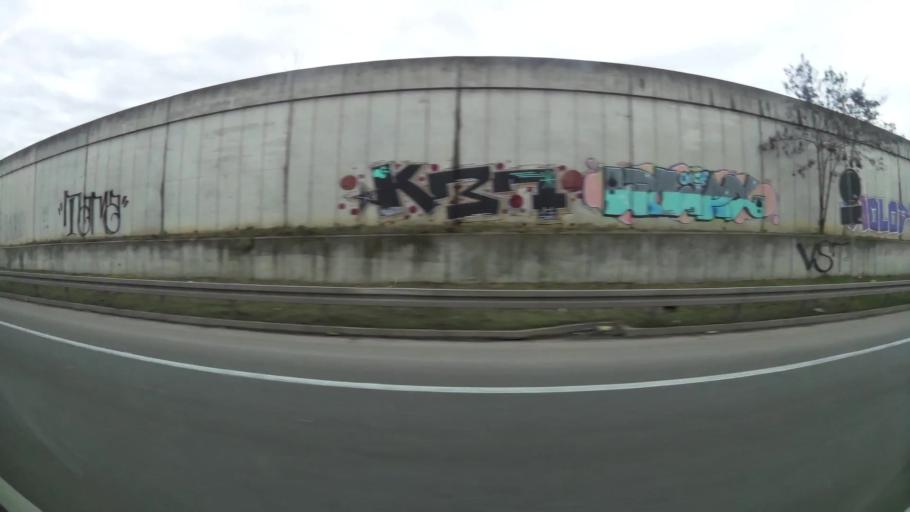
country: RS
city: Ostruznica
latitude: 44.7255
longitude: 20.3555
